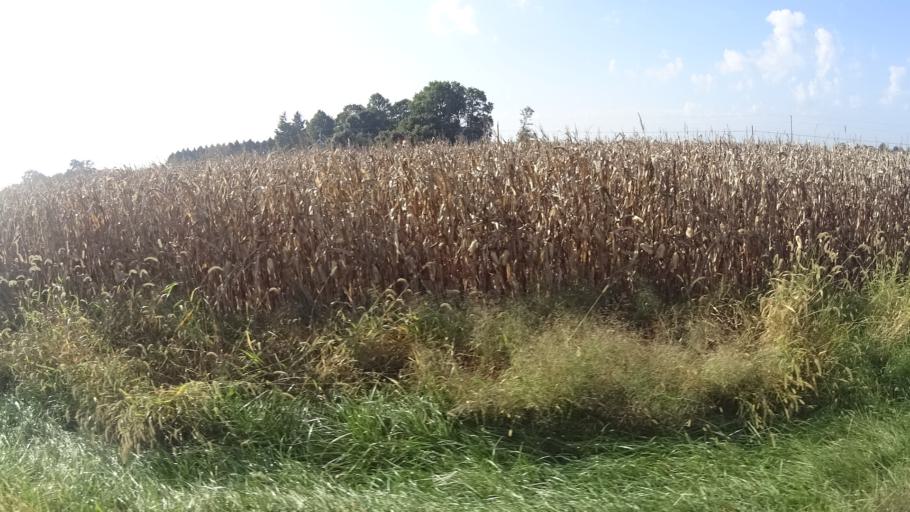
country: US
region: Indiana
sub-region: Madison County
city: Lapel
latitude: 40.0602
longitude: -85.8363
